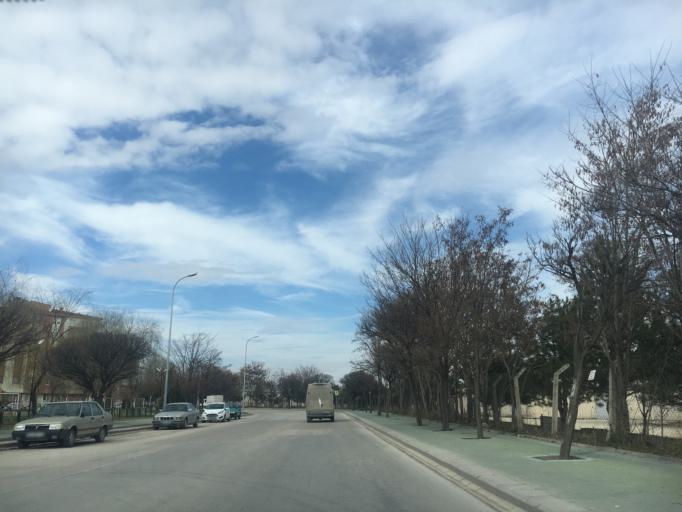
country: TR
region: Eskisehir
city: Eskisehir
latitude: 39.7793
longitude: 30.5340
